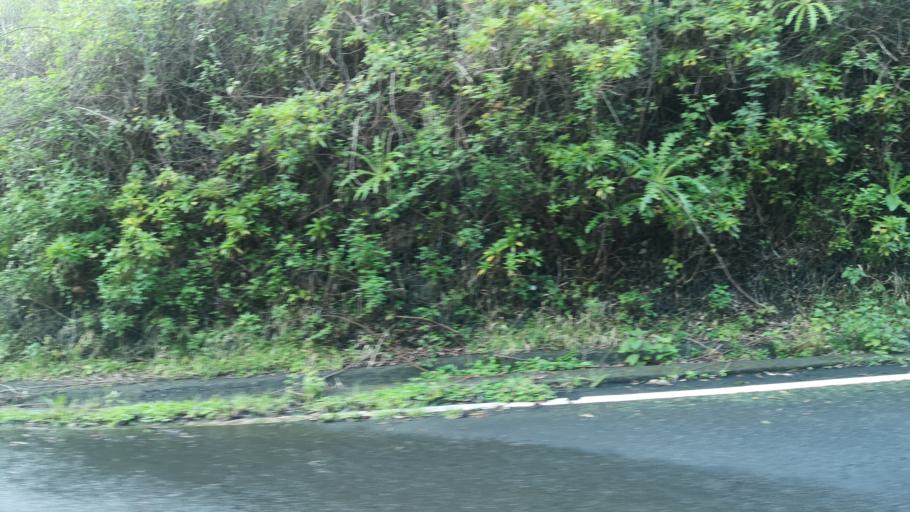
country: ES
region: Canary Islands
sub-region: Provincia de Santa Cruz de Tenerife
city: Hermigua
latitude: 28.1304
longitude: -17.2106
